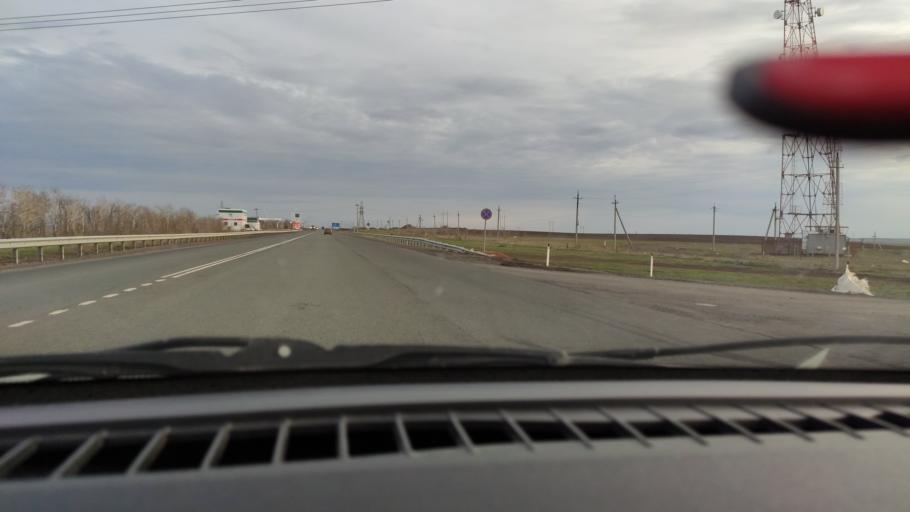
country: RU
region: Orenburg
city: Tatarskaya Kargala
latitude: 51.9792
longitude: 55.1872
